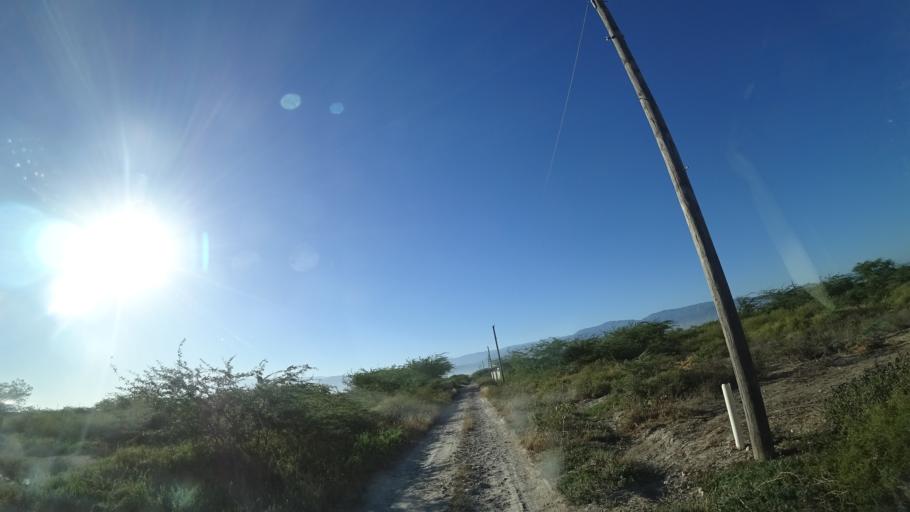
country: HT
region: Ouest
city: Croix des Bouquets
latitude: 18.6559
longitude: -72.2246
